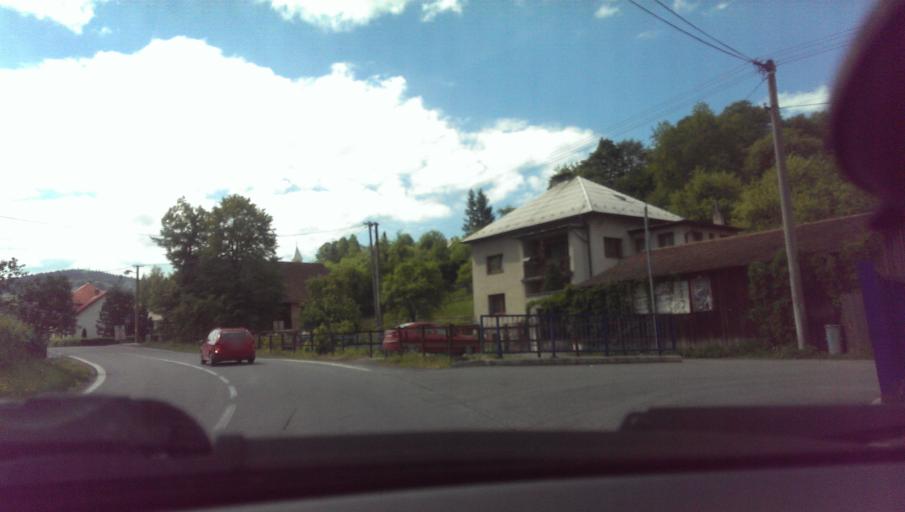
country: CZ
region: Zlin
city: Valasska Polanka
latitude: 49.2371
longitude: 17.9539
